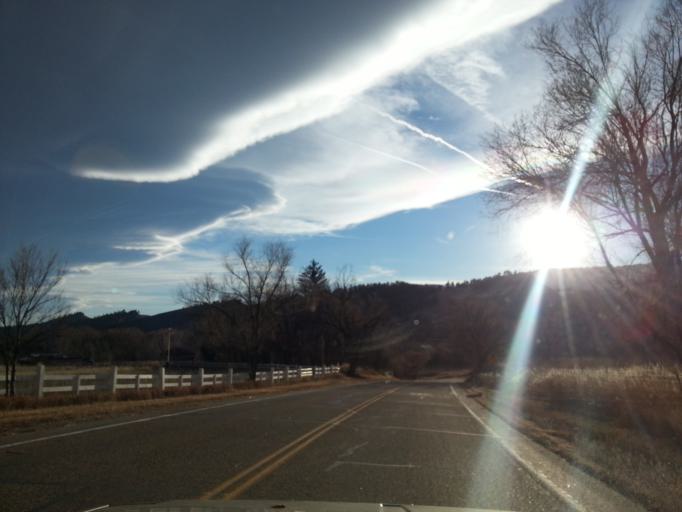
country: US
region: Colorado
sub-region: Larimer County
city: Loveland
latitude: 40.4831
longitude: -105.2111
